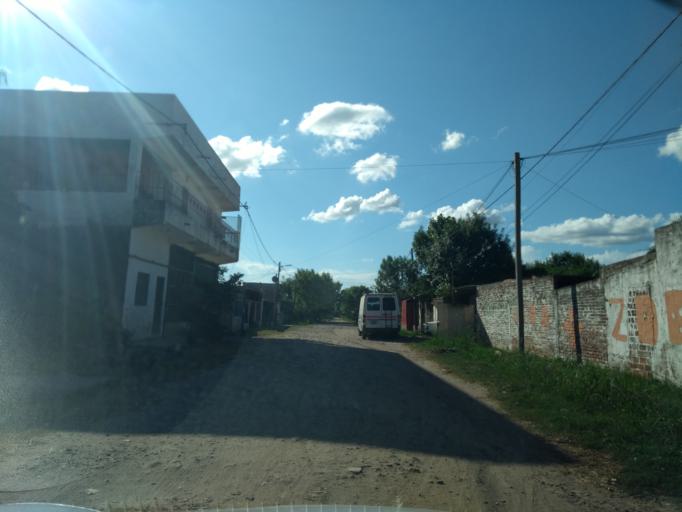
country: AR
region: Chaco
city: Resistencia
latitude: -27.4795
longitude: -58.9771
